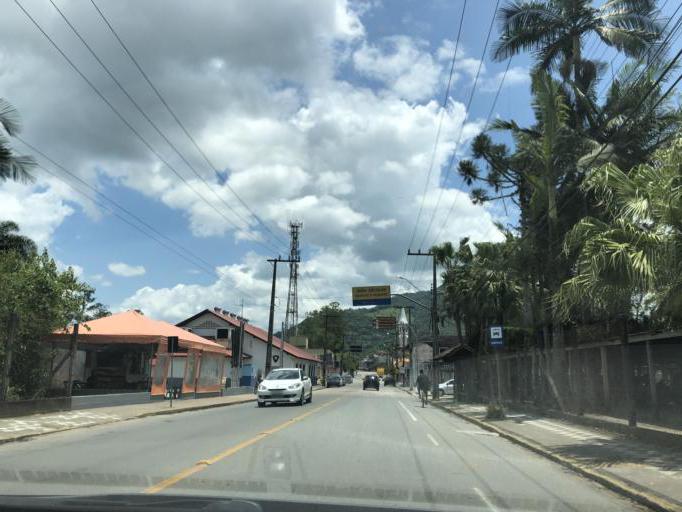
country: BR
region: Santa Catarina
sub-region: Jaragua Do Sul
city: Jaragua do Sul
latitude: -26.5140
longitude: -49.1271
